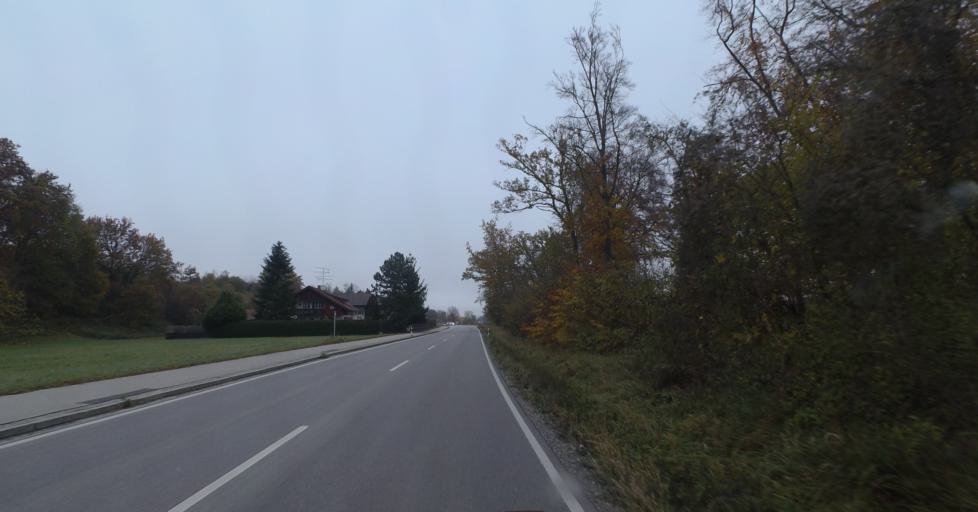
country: DE
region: Bavaria
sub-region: Upper Bavaria
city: Trostberg an der Alz
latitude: 48.0431
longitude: 12.5626
